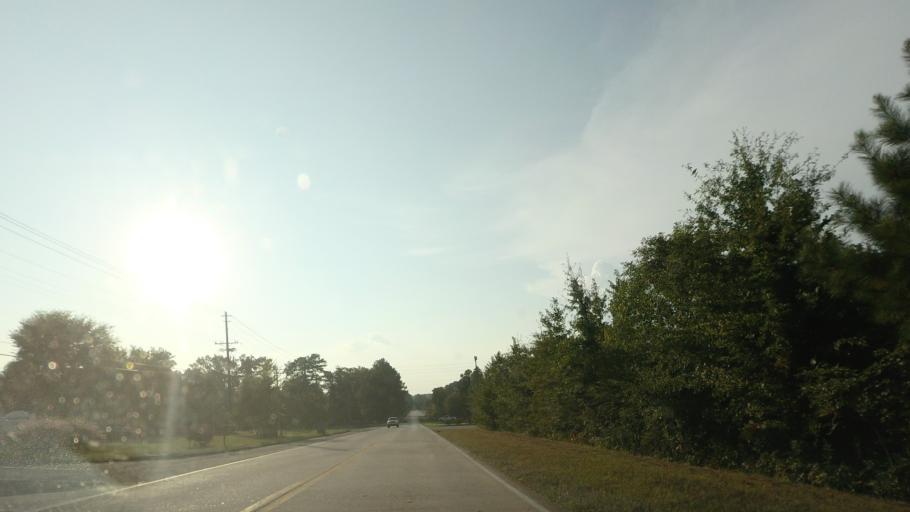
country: US
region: Georgia
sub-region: Bibb County
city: Macon
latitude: 32.9342
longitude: -83.7226
